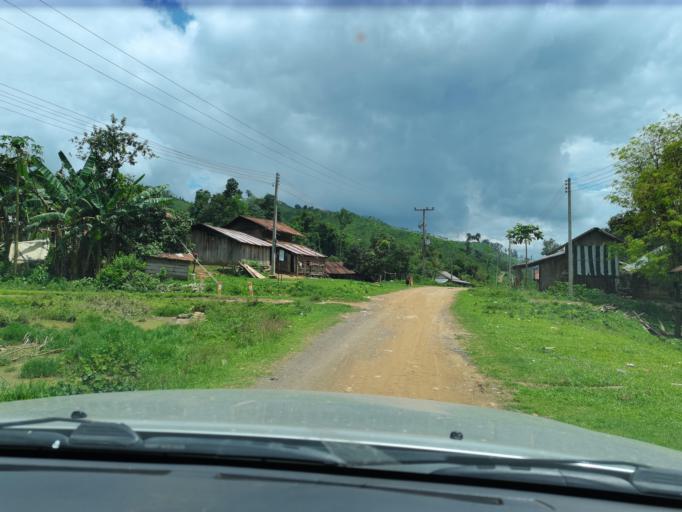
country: LA
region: Loungnamtha
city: Muang Long
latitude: 20.7242
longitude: 101.0143
